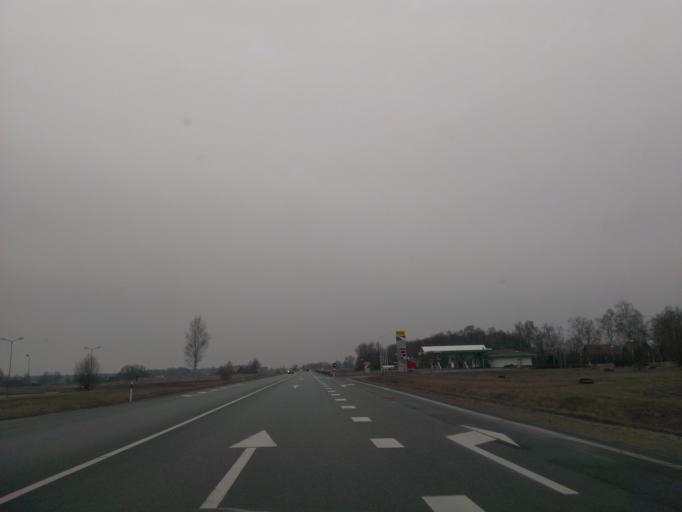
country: LV
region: Adazi
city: Adazi
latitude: 57.0877
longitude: 24.3139
